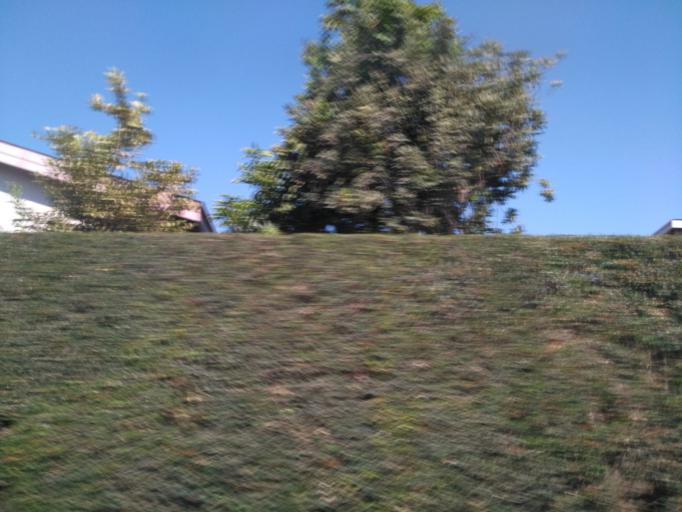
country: TZ
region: Dodoma
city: Dodoma
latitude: -6.1632
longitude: 35.7532
